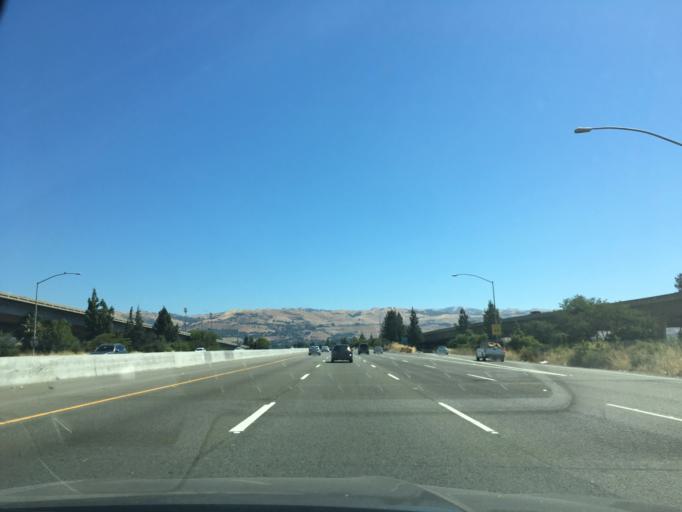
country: US
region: California
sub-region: Santa Clara County
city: Alum Rock
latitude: 37.3401
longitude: -121.8511
